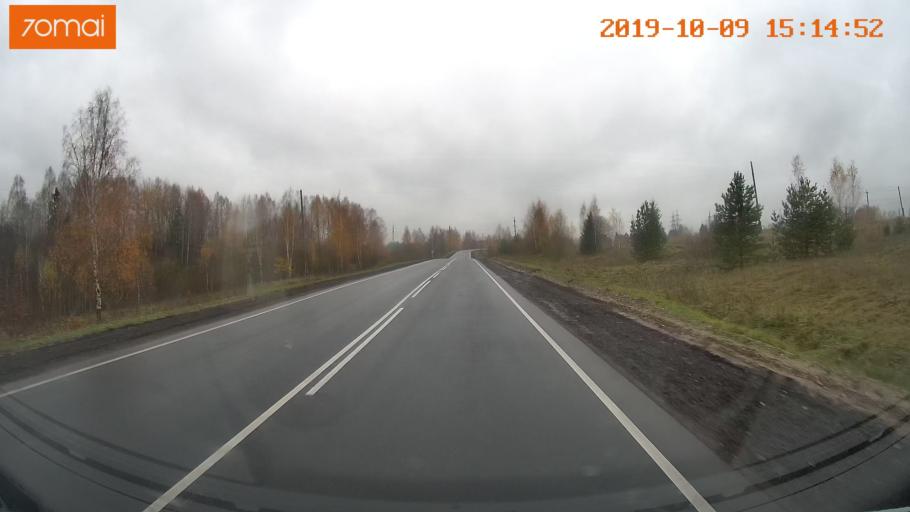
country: RU
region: Kostroma
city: Susanino
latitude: 58.1288
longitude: 41.5997
